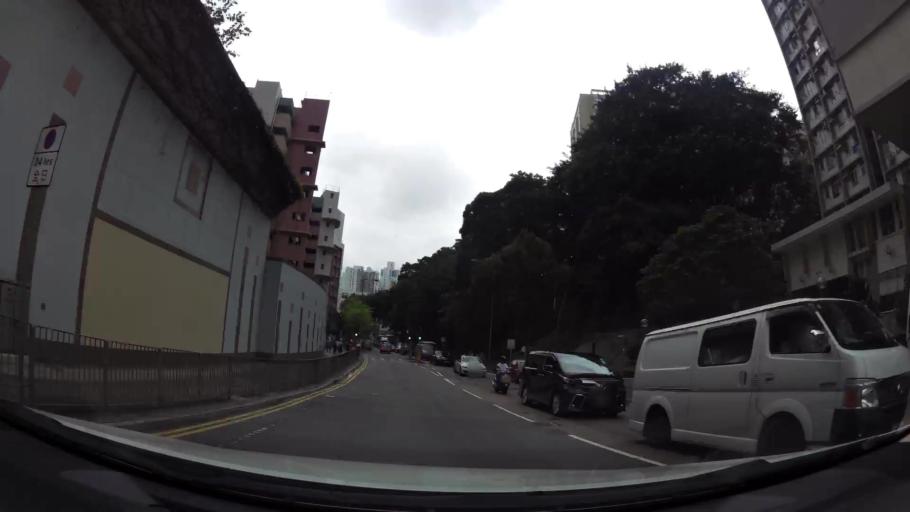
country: HK
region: Wong Tai Sin
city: Wong Tai Sin
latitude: 22.3434
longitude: 114.1919
